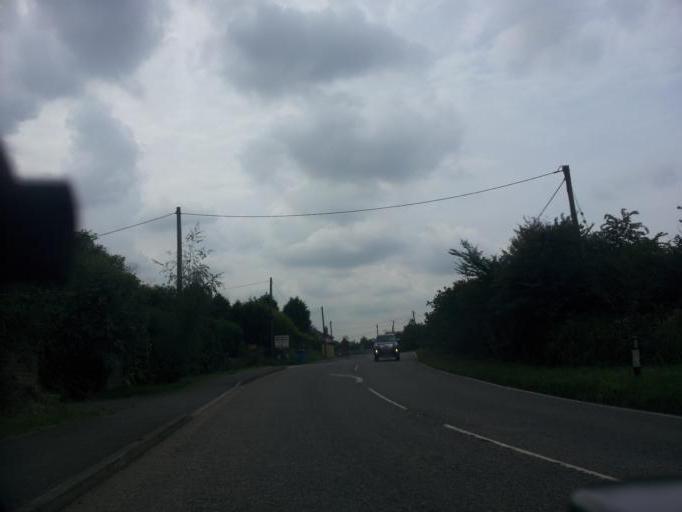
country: GB
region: England
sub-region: Kent
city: Sittingbourne
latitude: 51.3619
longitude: 0.7241
